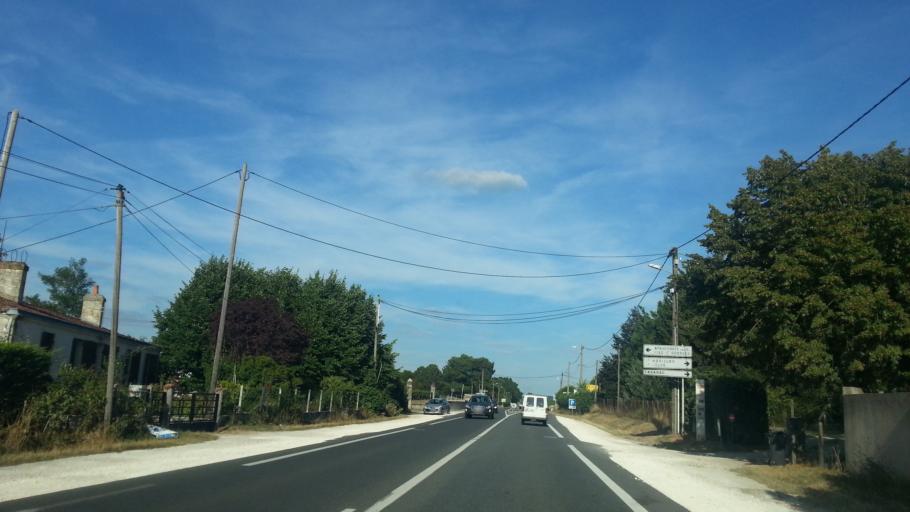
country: FR
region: Aquitaine
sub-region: Departement de la Gironde
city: Ayguemorte-les-Graves
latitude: 44.6962
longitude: -0.4846
